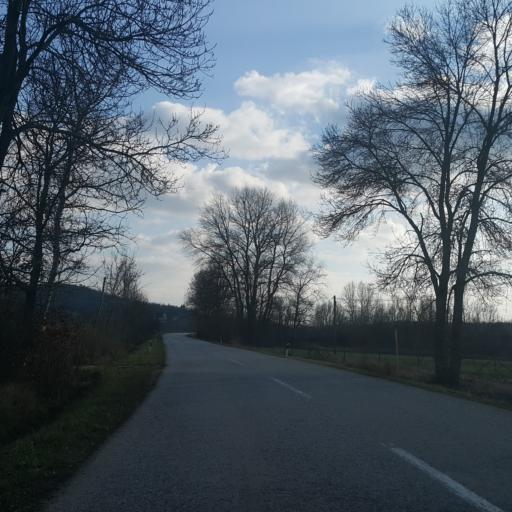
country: RS
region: Central Serbia
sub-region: Sumadijski Okrug
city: Topola
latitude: 44.2505
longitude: 20.8297
